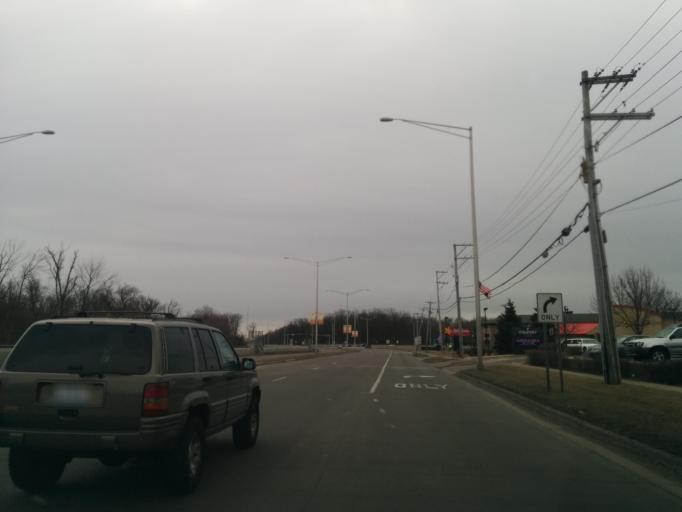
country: US
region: Illinois
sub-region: Cook County
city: Prospect Heights
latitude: 42.1065
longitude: -87.8887
